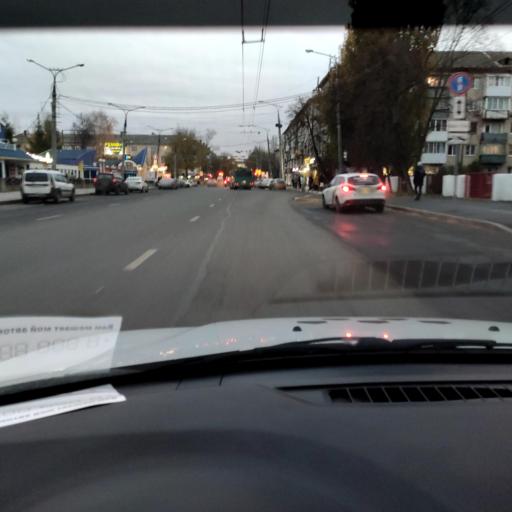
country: RU
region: Samara
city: Tol'yatti
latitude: 53.5098
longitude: 49.4153
